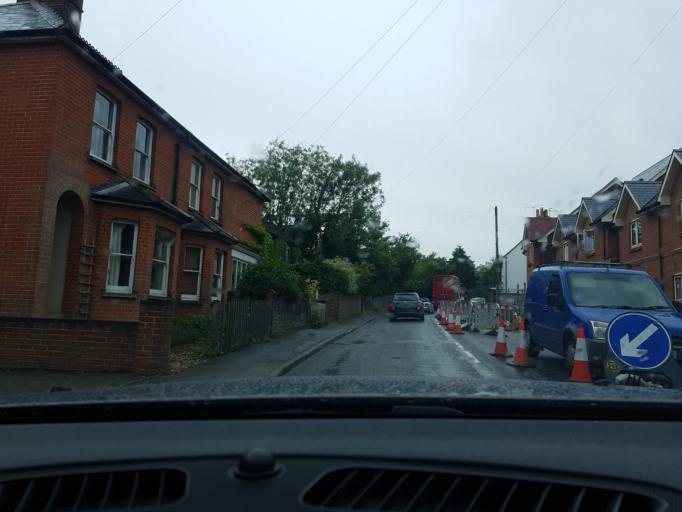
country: GB
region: England
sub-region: Surrey
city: Hale
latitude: 51.2316
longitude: -0.7903
